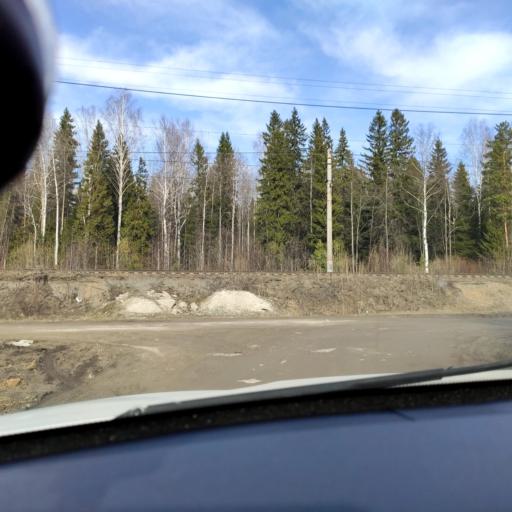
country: RU
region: Perm
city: Overyata
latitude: 58.0603
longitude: 55.9881
